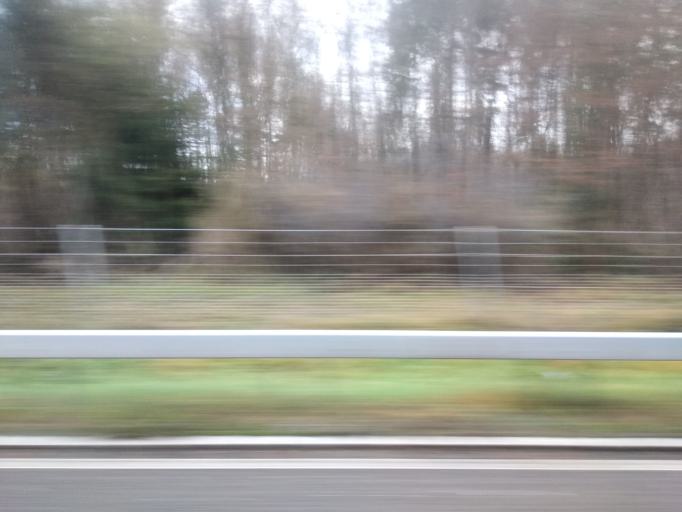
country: CH
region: Saint Gallen
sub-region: Wahlkreis Wil
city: Wil
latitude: 47.4563
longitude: 9.0689
